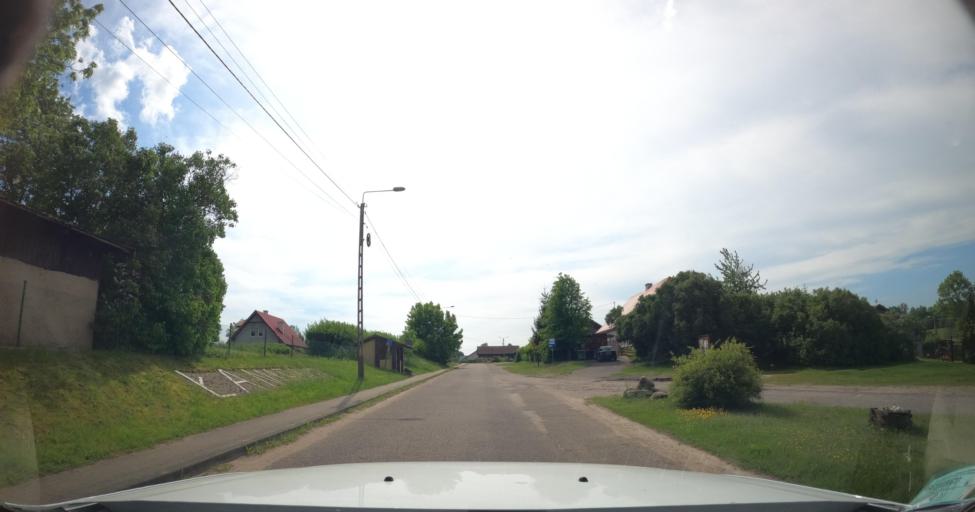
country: PL
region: Warmian-Masurian Voivodeship
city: Dobre Miasto
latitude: 54.0981
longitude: 20.4471
